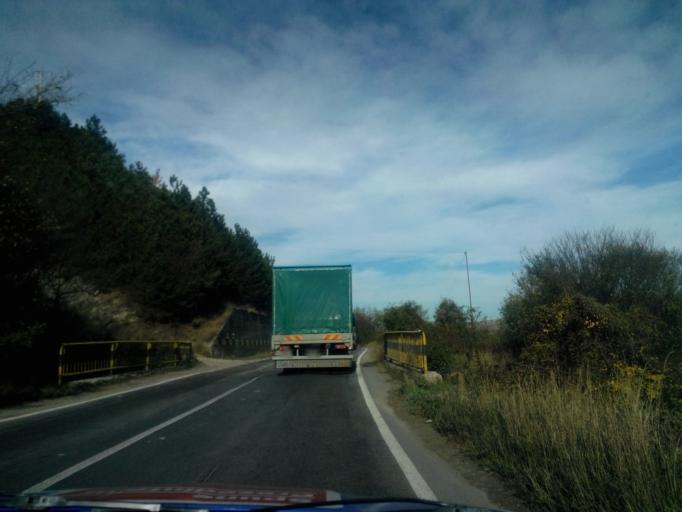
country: RO
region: Bacau
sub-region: Comuna Helegiu
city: Bratila
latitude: 46.3085
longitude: 26.7503
